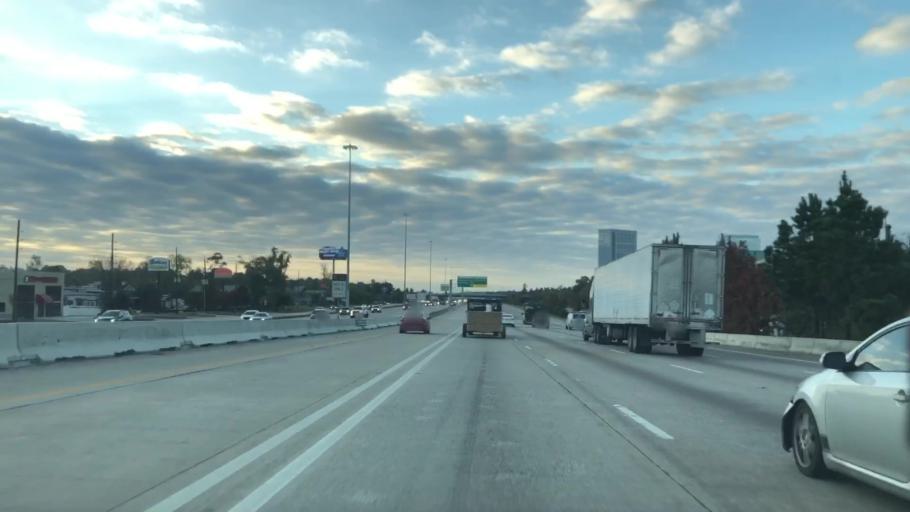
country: US
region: Texas
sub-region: Montgomery County
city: Shenandoah
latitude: 30.1750
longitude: -95.4516
